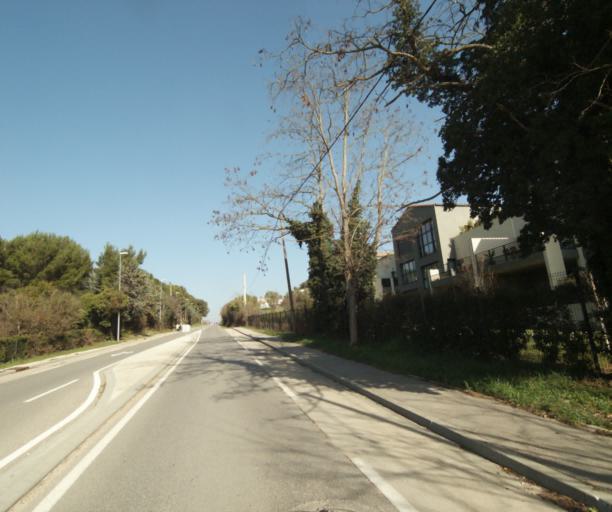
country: FR
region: Provence-Alpes-Cote d'Azur
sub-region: Departement des Bouches-du-Rhone
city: Bouc-Bel-Air
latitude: 43.4897
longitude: 5.4262
